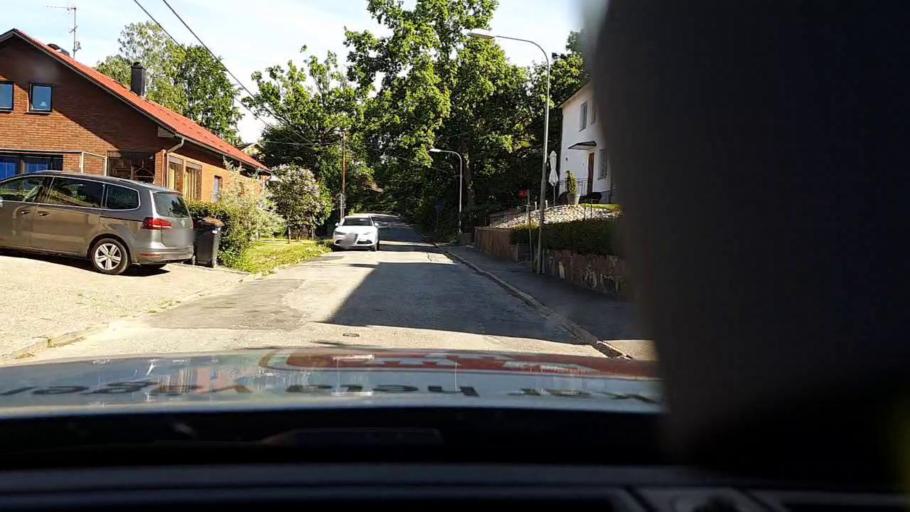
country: SE
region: Stockholm
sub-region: Stockholms Kommun
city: Arsta
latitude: 59.2692
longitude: 18.0238
